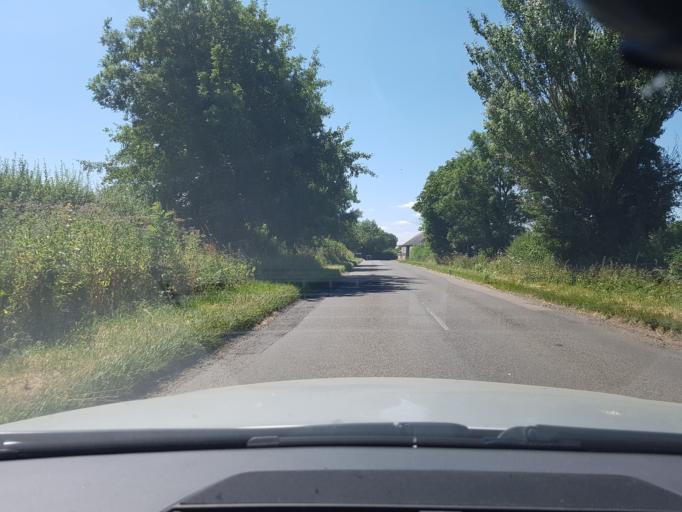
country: GB
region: England
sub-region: Milton Keynes
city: Calverton
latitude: 52.0332
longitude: -0.8312
